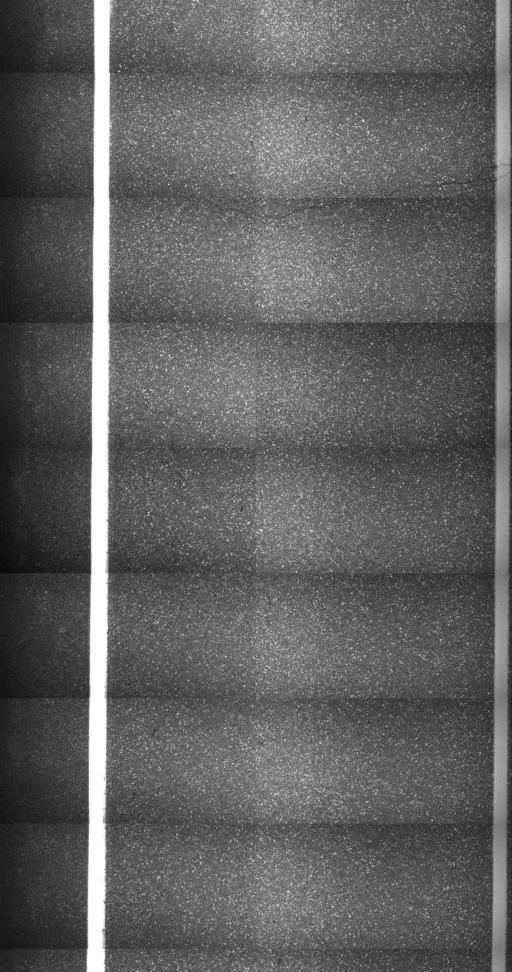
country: US
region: Vermont
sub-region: Orange County
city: Chelsea
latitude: 44.1191
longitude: -72.3075
